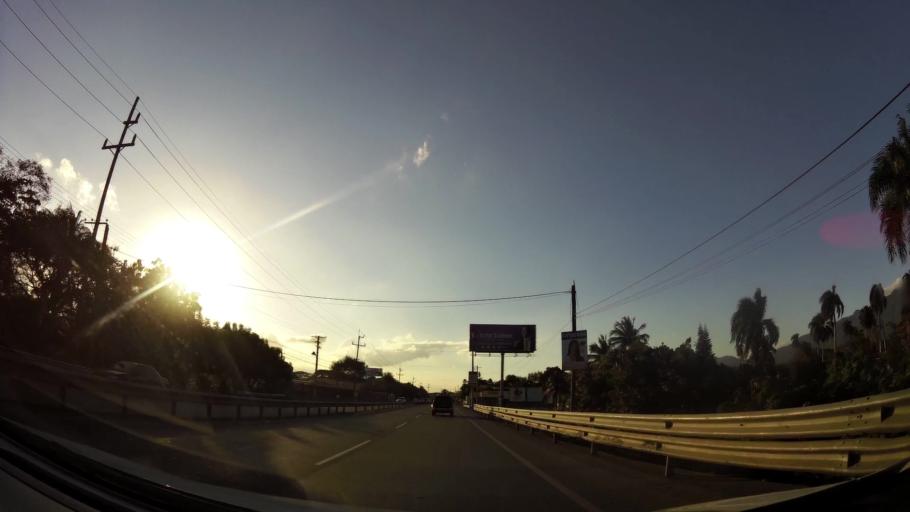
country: DO
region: Santiago
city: Palmar Arriba
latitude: 19.5032
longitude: -70.7487
